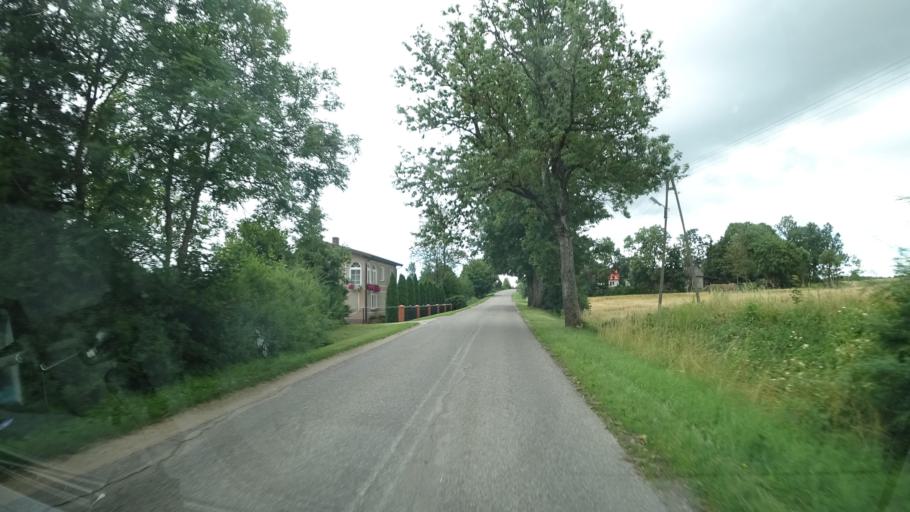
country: PL
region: Podlasie
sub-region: Powiat suwalski
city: Filipow
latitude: 54.2886
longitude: 22.5147
